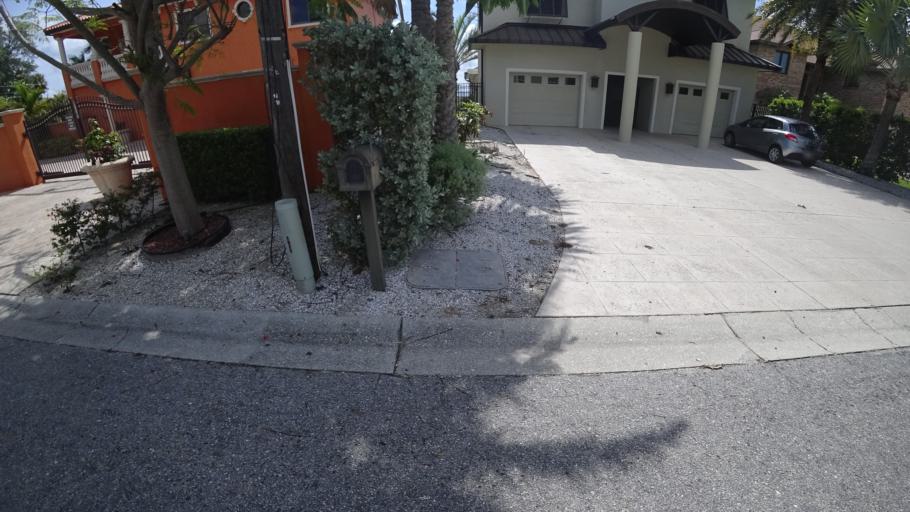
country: US
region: Florida
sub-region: Manatee County
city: West Bradenton
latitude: 27.5131
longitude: -82.6205
